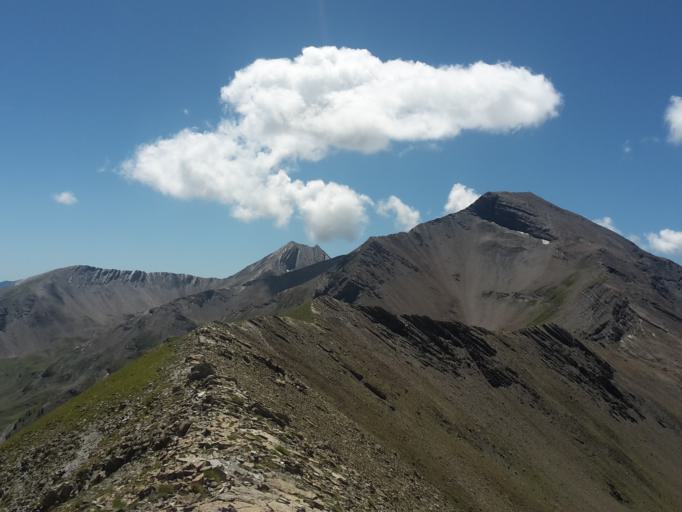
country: FR
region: Provence-Alpes-Cote d'Azur
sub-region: Departement des Hautes-Alpes
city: Embrun
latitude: 44.6575
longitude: 6.4214
